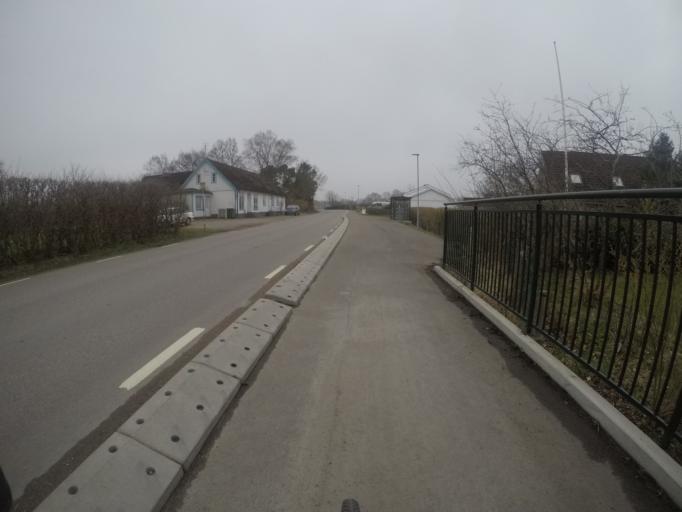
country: SE
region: Skane
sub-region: Angelholms Kommun
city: Vejbystrand
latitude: 56.2189
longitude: 12.7142
